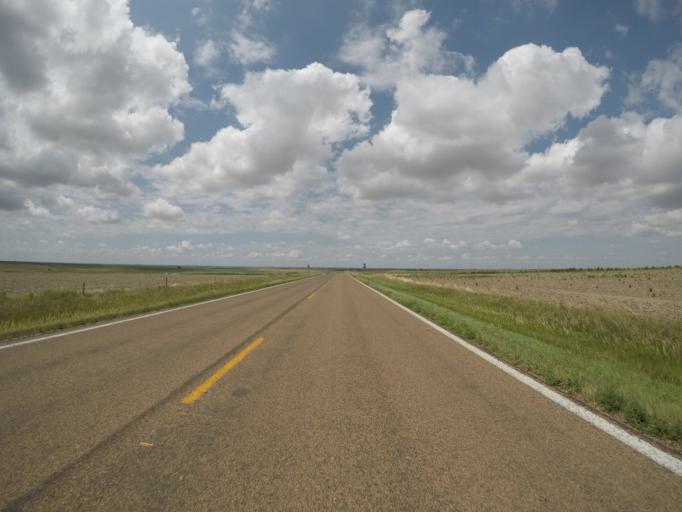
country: US
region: Kansas
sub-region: Rawlins County
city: Atwood
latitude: 39.9068
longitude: -101.0507
